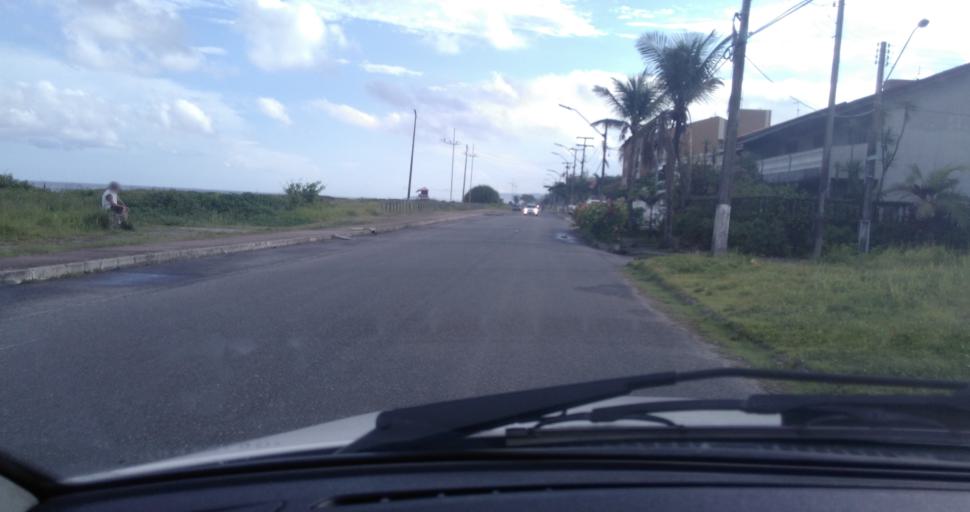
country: BR
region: Parana
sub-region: Pontal Do Parana
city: Pontal do Parana
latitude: -25.7343
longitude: -48.4910
